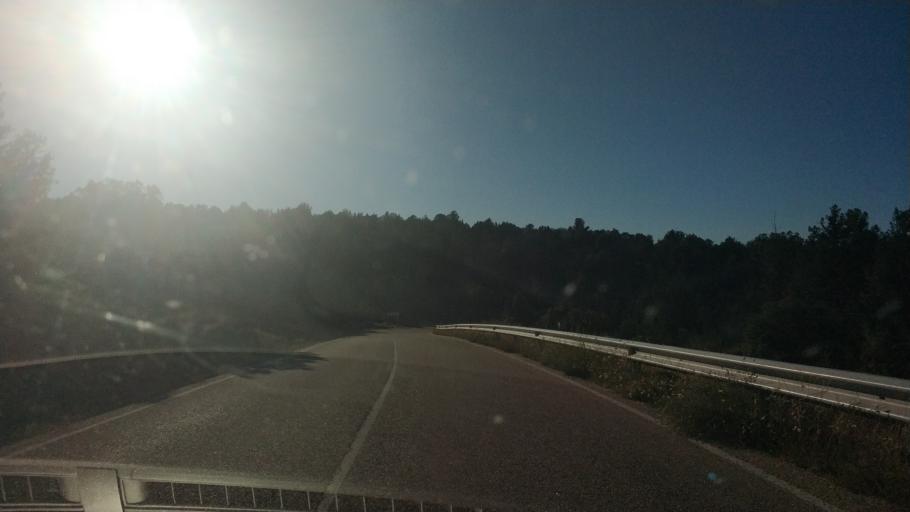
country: ES
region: Castille and Leon
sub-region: Provincia de Soria
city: Montejo de Tiermes
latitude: 41.4267
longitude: -3.2027
